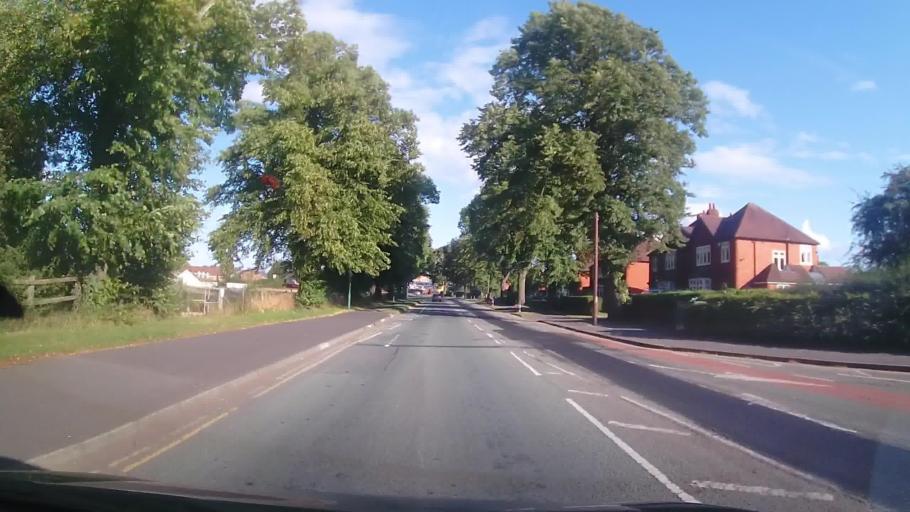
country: GB
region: England
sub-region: Shropshire
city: Bayston Hill
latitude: 52.6894
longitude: -2.7447
